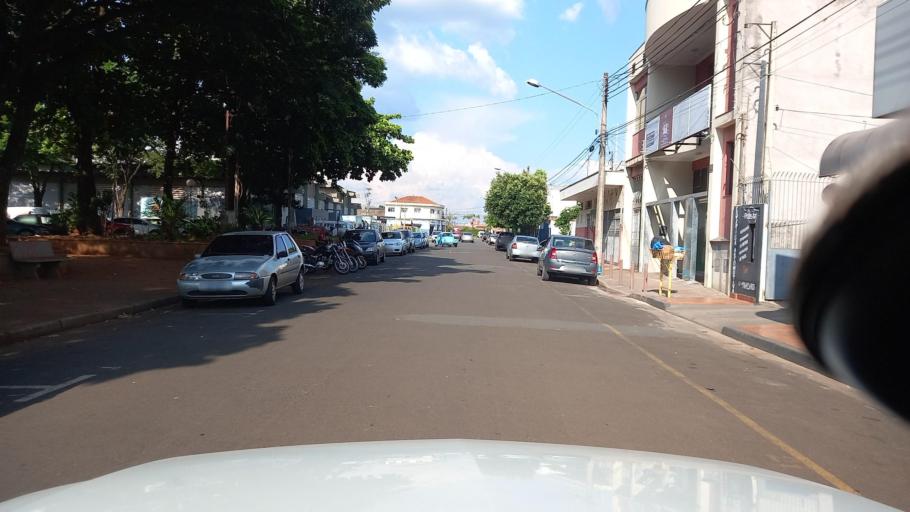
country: BR
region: Sao Paulo
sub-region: Moji-Guacu
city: Mogi-Gaucu
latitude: -22.3511
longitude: -46.9477
